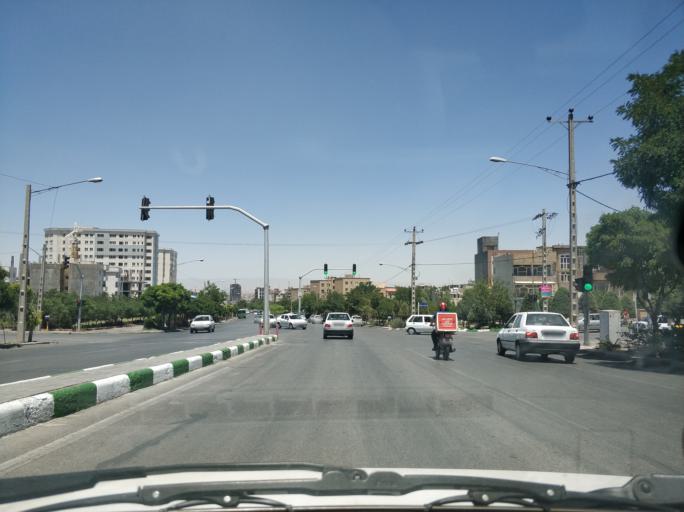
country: IR
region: Razavi Khorasan
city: Mashhad
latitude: 36.2971
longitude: 59.5083
